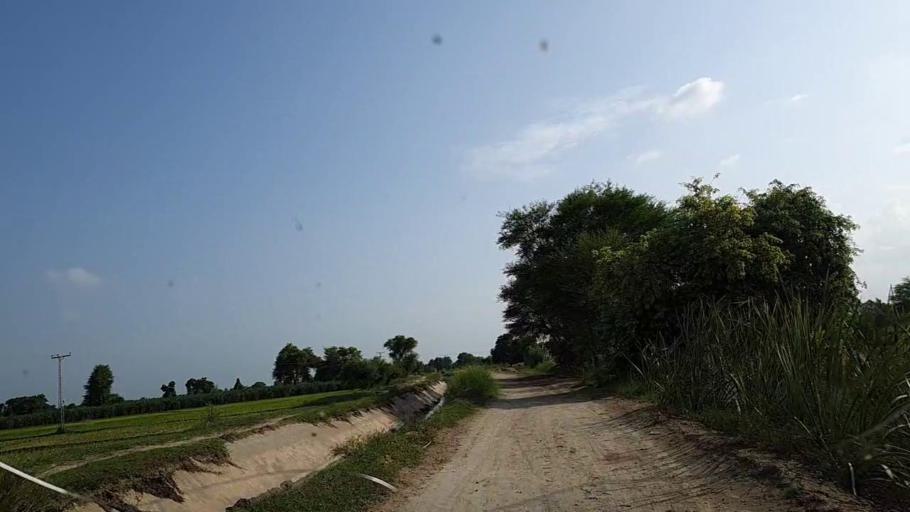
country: PK
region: Sindh
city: Bhiria
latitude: 26.8642
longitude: 68.2529
